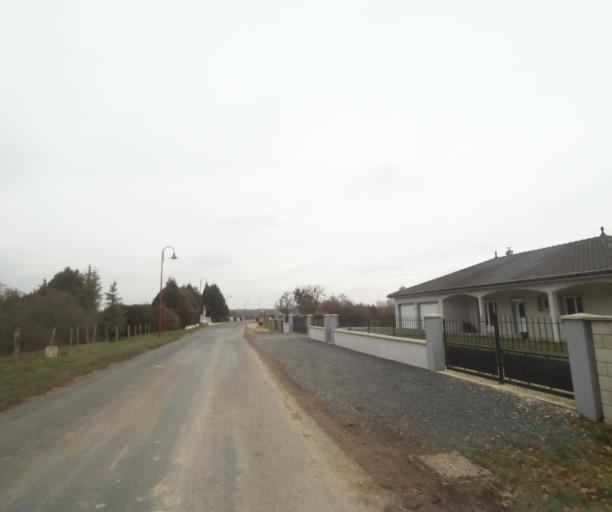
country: FR
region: Champagne-Ardenne
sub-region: Departement de la Marne
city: Pargny-sur-Saulx
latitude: 48.7459
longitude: 4.8424
